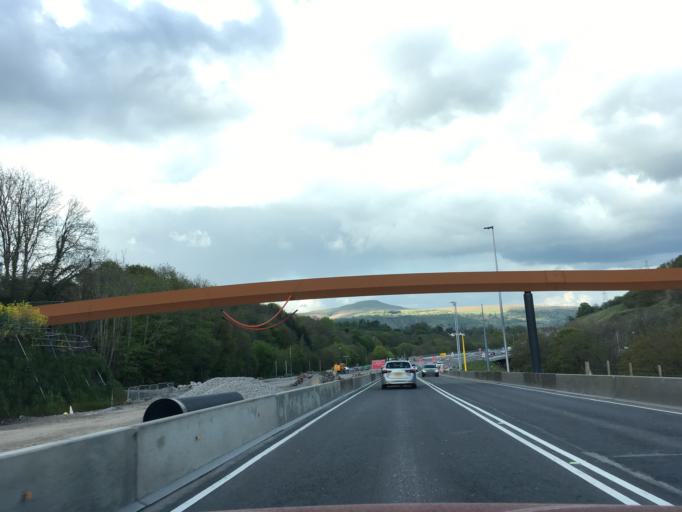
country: GB
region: Wales
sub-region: Monmouthshire
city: Gilwern
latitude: 51.8145
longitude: -3.1188
